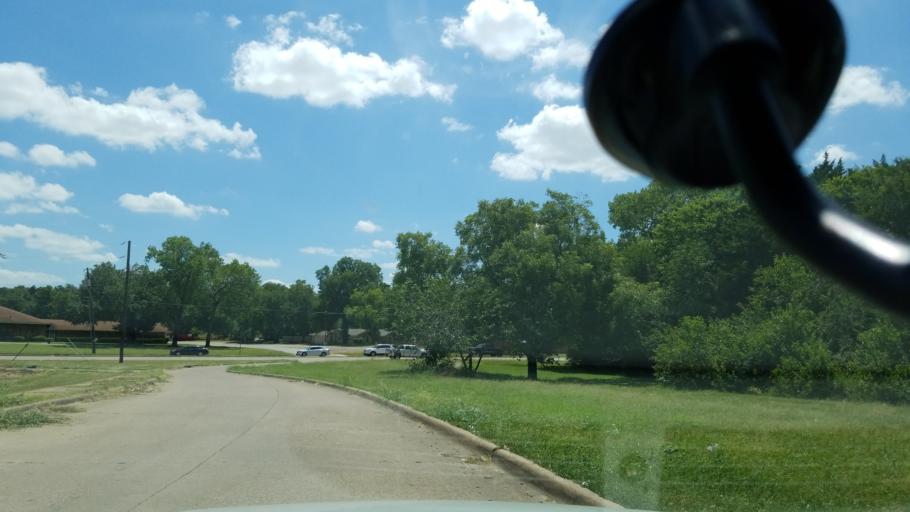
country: US
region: Texas
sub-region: Dallas County
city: Cockrell Hill
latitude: 32.6904
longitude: -96.8302
